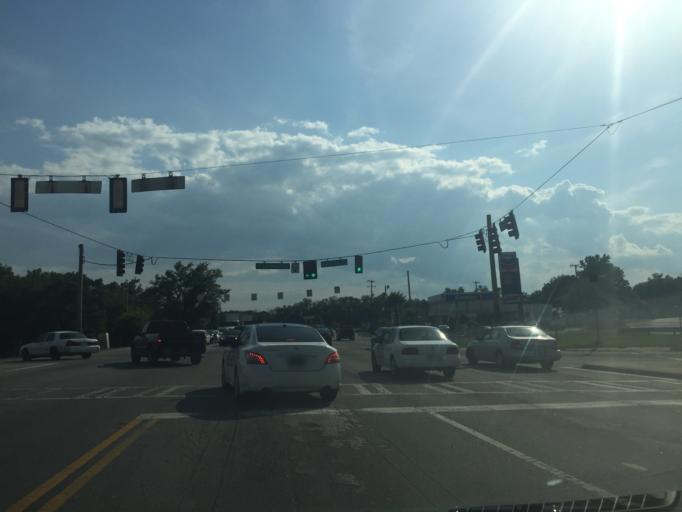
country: US
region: Georgia
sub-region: Chatham County
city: Garden City
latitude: 32.0871
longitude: -81.1590
